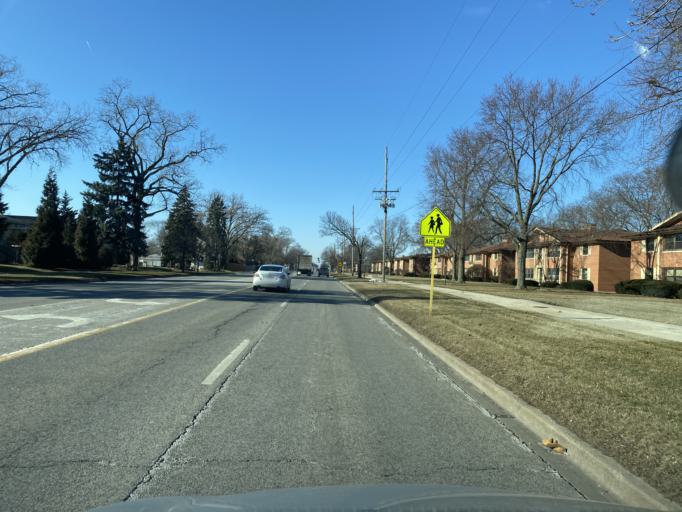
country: US
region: Illinois
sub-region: Cook County
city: Westchester
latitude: 41.8486
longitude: -87.8879
